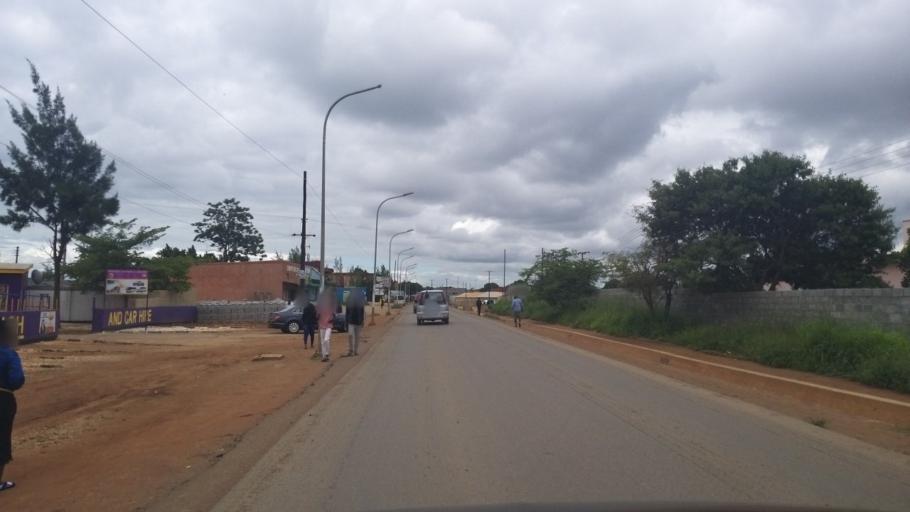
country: ZM
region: Lusaka
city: Lusaka
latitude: -15.4429
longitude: 28.3081
